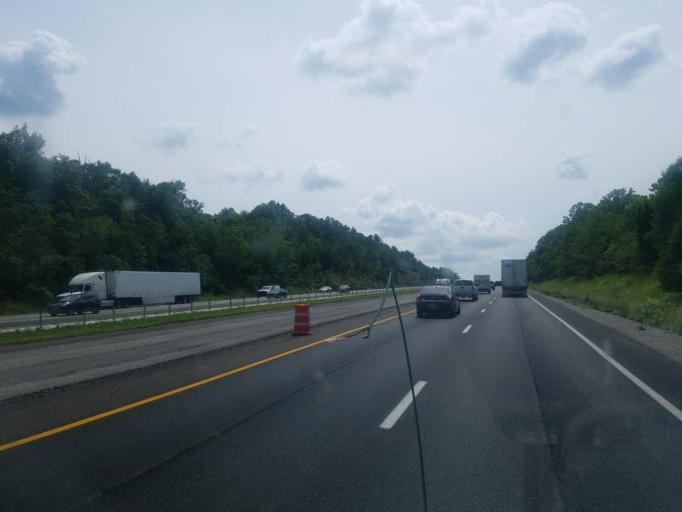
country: US
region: Kentucky
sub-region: Hardin County
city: Elizabethtown
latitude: 37.7354
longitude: -85.8082
